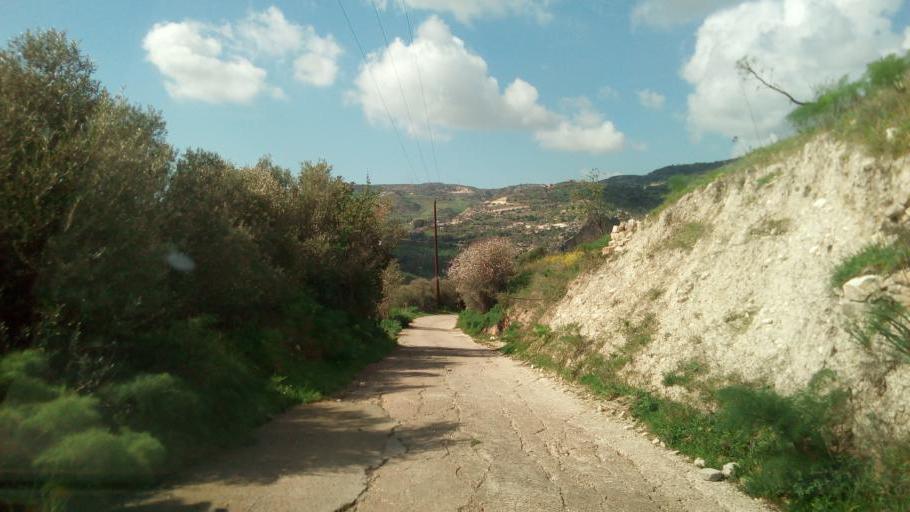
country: CY
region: Pafos
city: Mesogi
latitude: 34.7912
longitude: 32.5373
